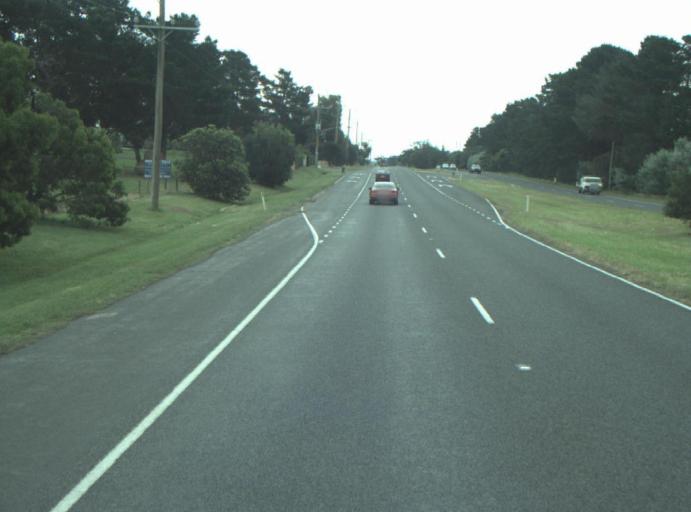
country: AU
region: Victoria
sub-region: Greater Geelong
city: Clifton Springs
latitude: -38.1843
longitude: 144.5399
